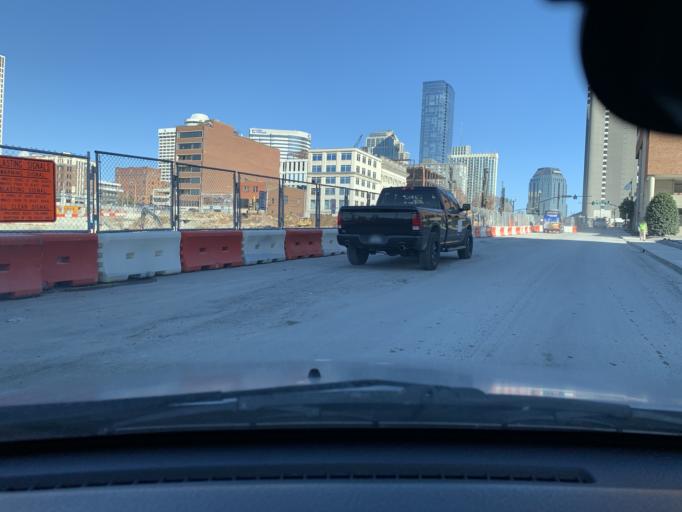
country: US
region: Tennessee
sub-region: Davidson County
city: Nashville
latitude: 36.1592
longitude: -86.7848
